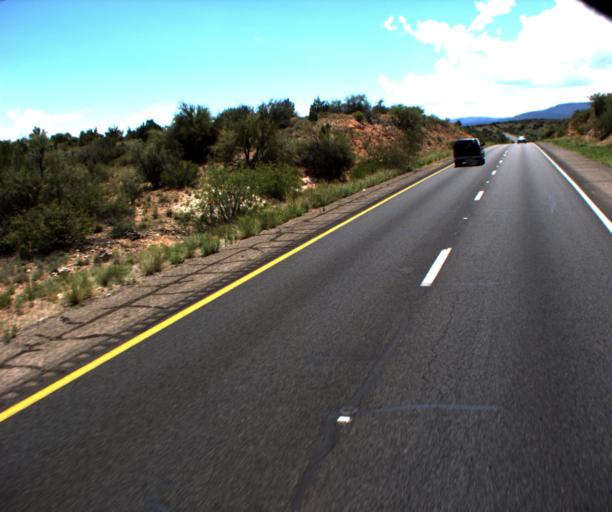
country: US
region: Arizona
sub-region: Yavapai County
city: Verde Village
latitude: 34.6733
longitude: -111.9713
